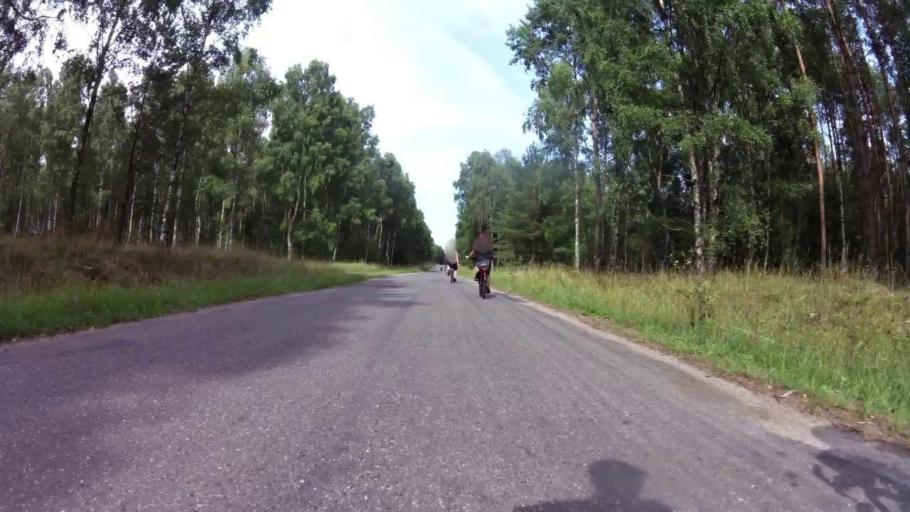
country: PL
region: West Pomeranian Voivodeship
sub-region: Powiat stargardzki
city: Insko
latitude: 53.4214
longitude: 15.6093
